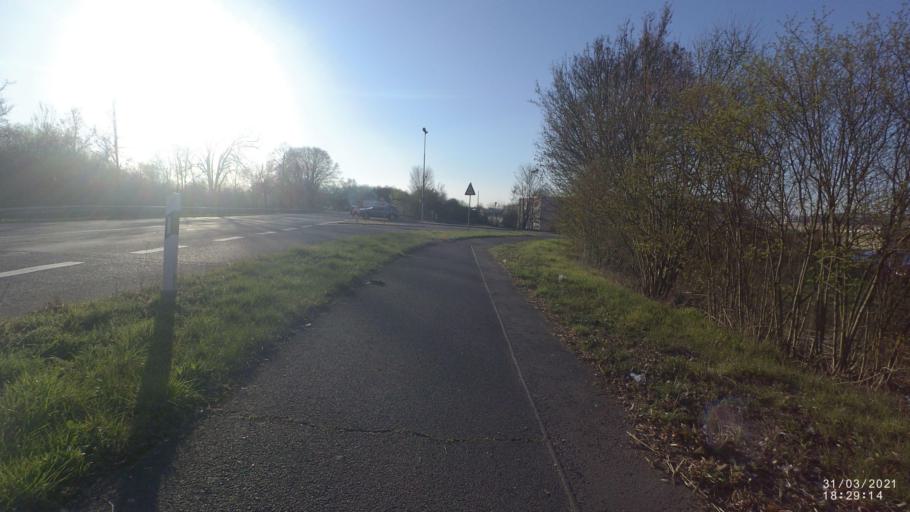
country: DE
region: Rheinland-Pfalz
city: Urmitz
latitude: 50.3982
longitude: 7.5207
